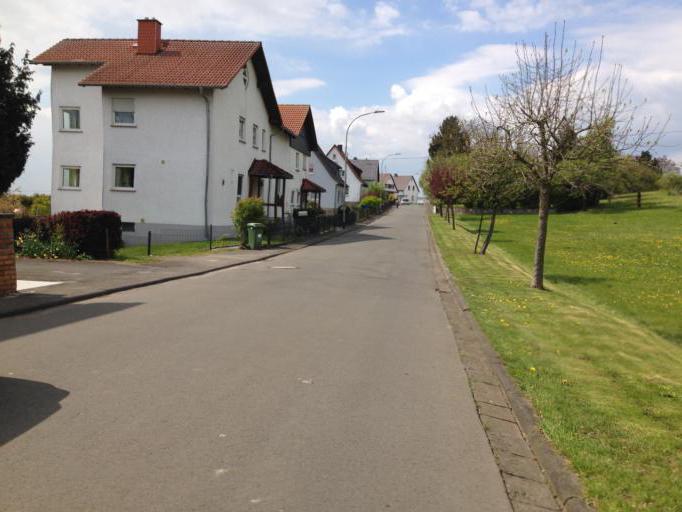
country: DE
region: Hesse
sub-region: Regierungsbezirk Giessen
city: Grunberg
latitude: 50.6083
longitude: 8.9888
